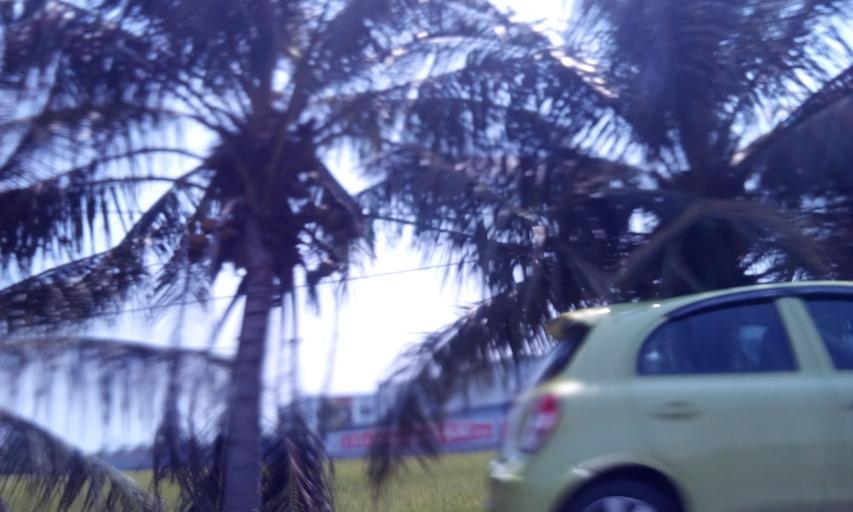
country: TH
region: Nonthaburi
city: Bang Bua Thong
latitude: 13.9095
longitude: 100.3744
